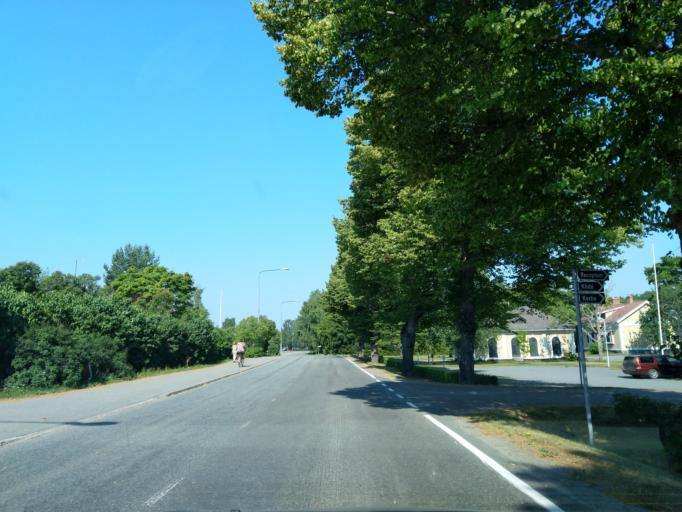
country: FI
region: Satakunta
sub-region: Pori
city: Noormarkku
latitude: 61.5922
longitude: 21.8761
